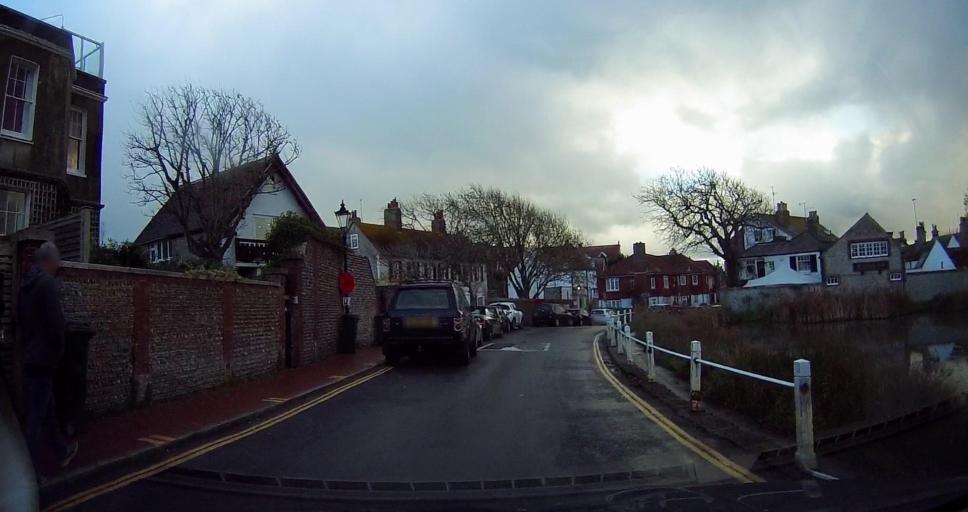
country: GB
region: England
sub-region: Brighton and Hove
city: Rottingdean
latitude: 50.8063
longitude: -0.0579
